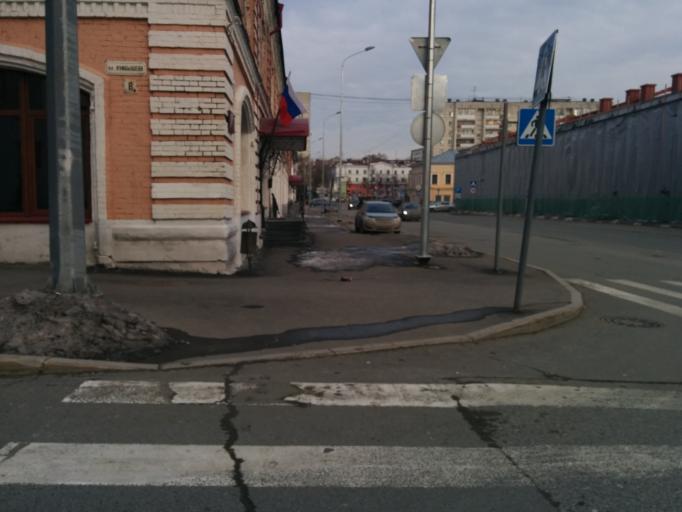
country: RU
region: Perm
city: Perm
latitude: 58.0136
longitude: 56.2322
